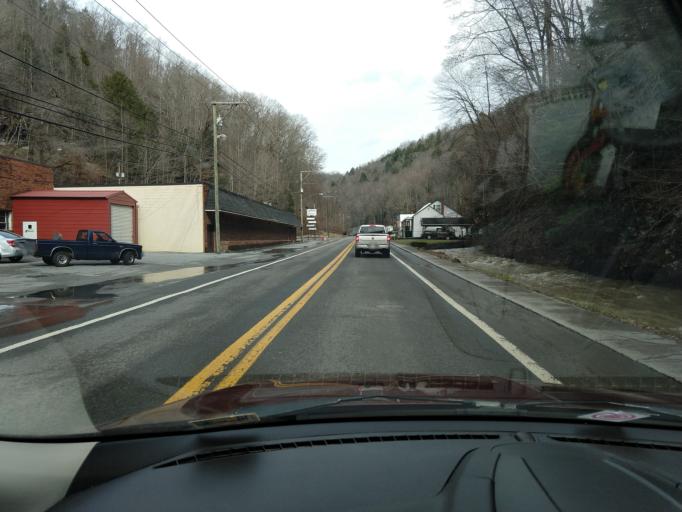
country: US
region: West Virginia
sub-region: McDowell County
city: Welch
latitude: 37.4467
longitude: -81.5651
